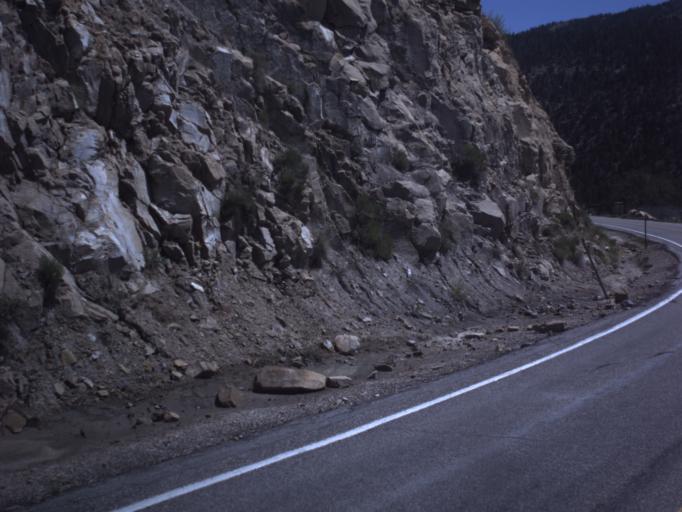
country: US
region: Utah
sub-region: Emery County
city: Orangeville
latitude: 39.2910
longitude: -111.2714
